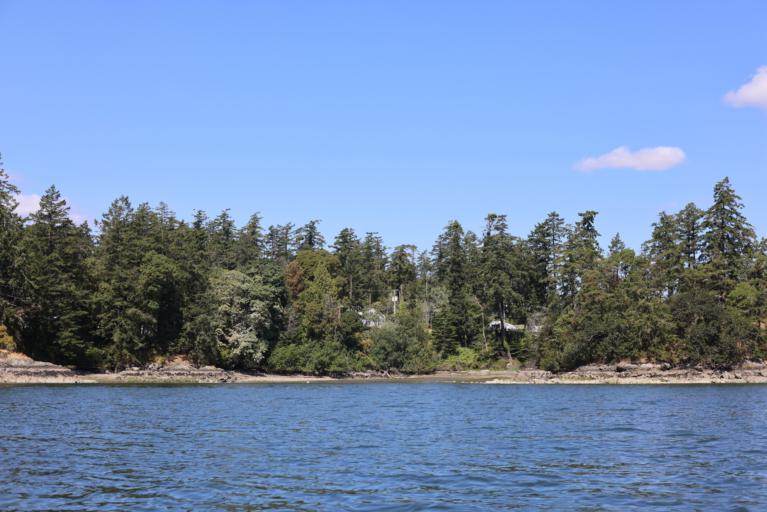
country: CA
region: British Columbia
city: Colwood
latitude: 48.4453
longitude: -123.4479
